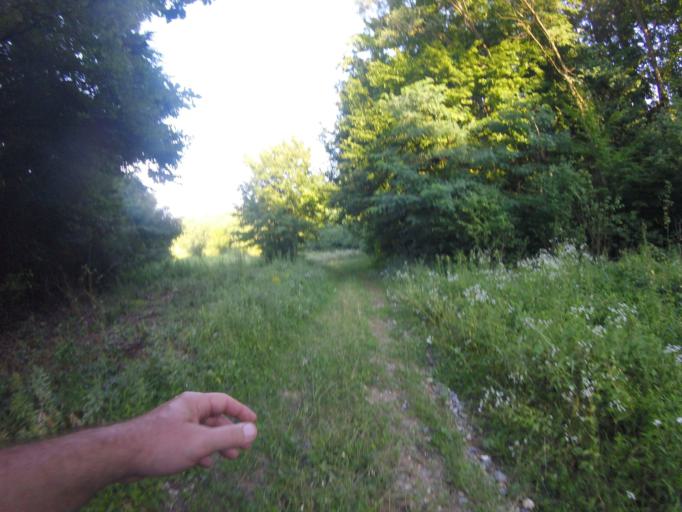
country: HU
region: Zala
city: Letenye
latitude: 46.5163
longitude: 16.7221
